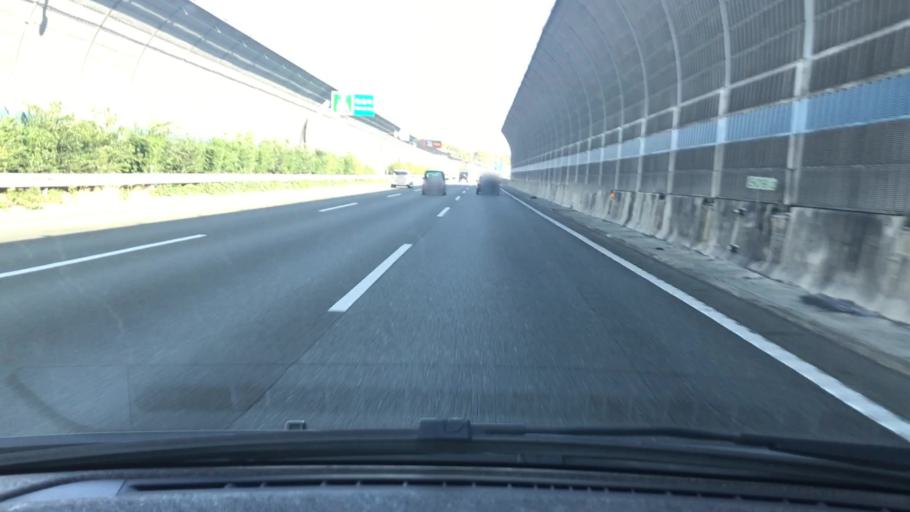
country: JP
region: Osaka
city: Ibaraki
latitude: 34.8470
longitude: 135.5776
